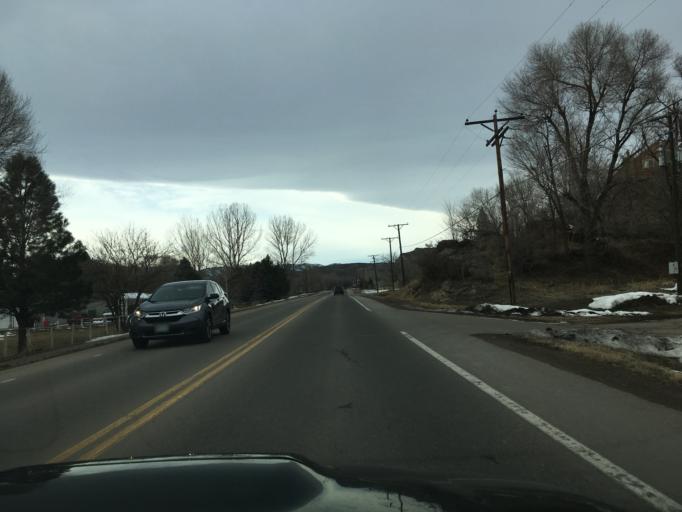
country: US
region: Colorado
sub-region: Larimer County
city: Laporte
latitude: 40.6306
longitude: -105.1482
